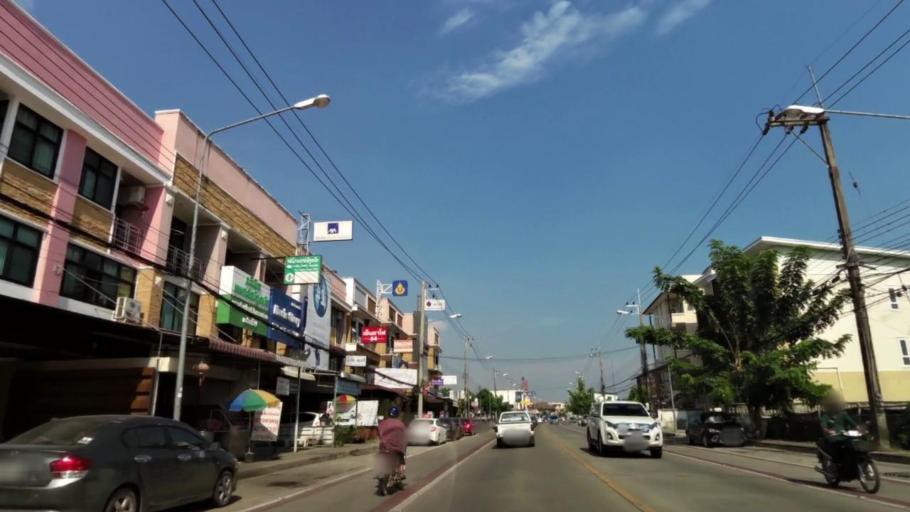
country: TH
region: Chiang Rai
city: Chiang Rai
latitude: 19.9230
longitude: 99.8344
